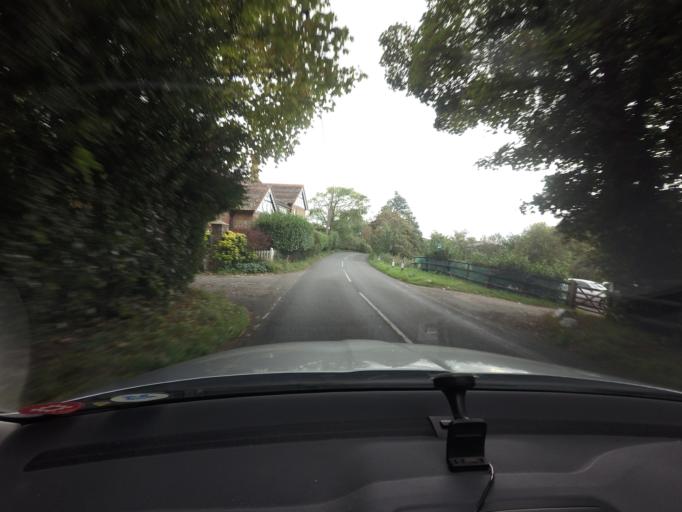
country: GB
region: England
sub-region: Kent
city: Borough Green
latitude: 51.2939
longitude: 0.2851
